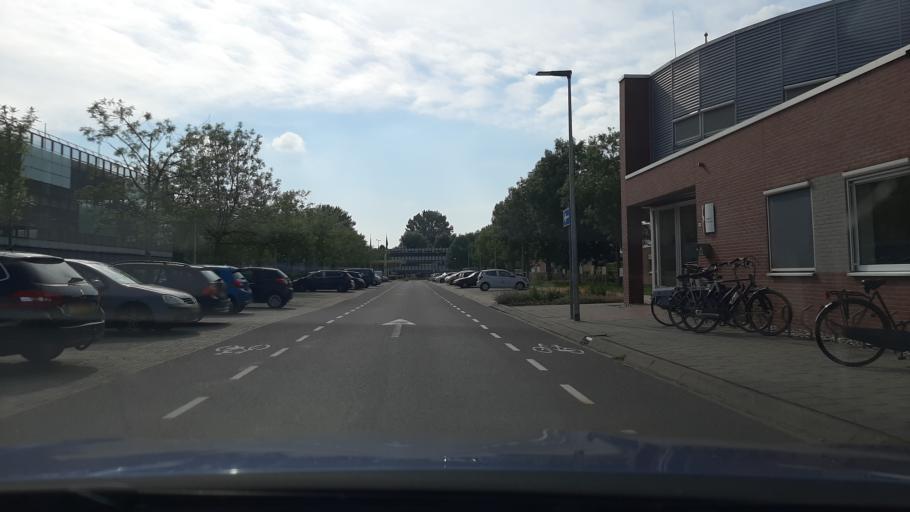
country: NL
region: Friesland
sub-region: Gemeente Leeuwarden
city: Huizum
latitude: 53.1891
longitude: 5.8025
